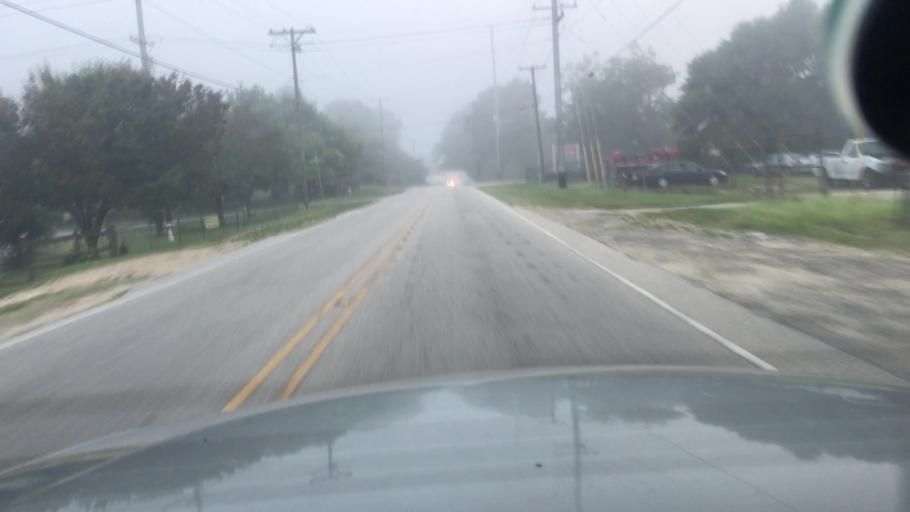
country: US
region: North Carolina
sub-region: Cumberland County
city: Fayetteville
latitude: 35.0141
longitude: -78.9033
